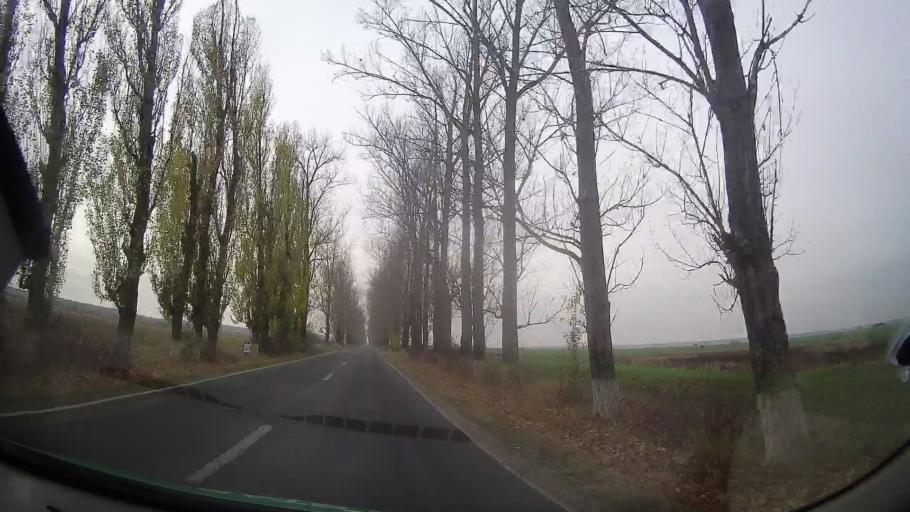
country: RO
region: Prahova
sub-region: Comuna Balta Doamnei
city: Balta Doamnei
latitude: 44.7442
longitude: 26.1633
